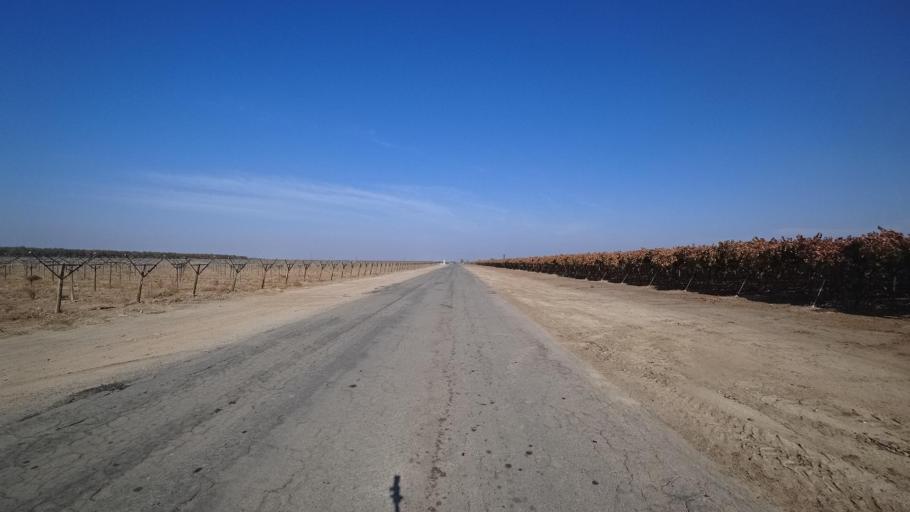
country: US
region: California
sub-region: Kern County
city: McFarland
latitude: 35.6251
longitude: -119.1866
